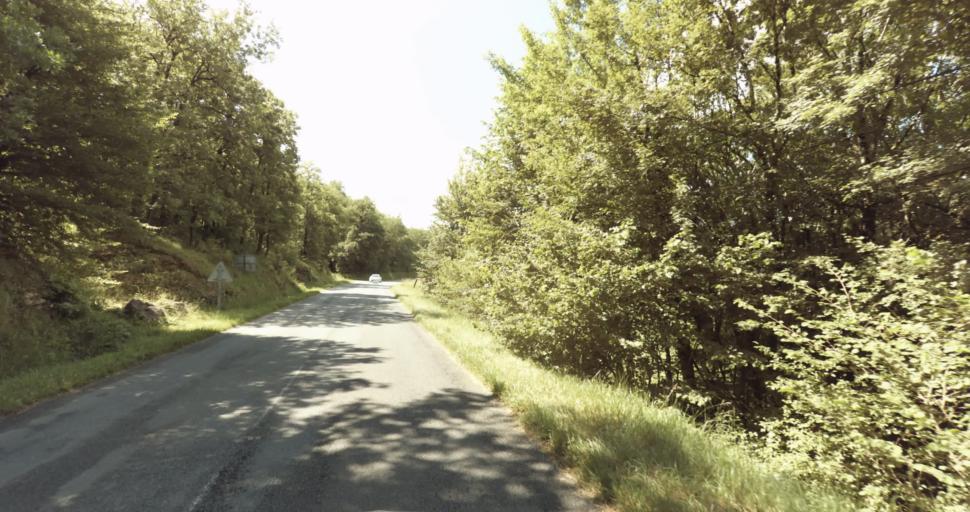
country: FR
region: Aquitaine
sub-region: Departement de la Dordogne
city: Le Bugue
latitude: 44.8347
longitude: 0.8990
